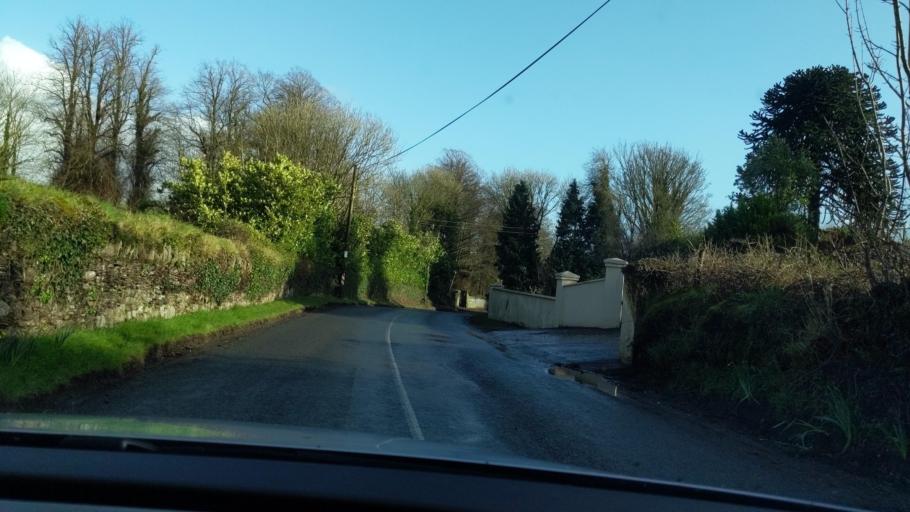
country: IE
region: Munster
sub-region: County Cork
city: Cork
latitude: 51.9262
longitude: -8.4964
